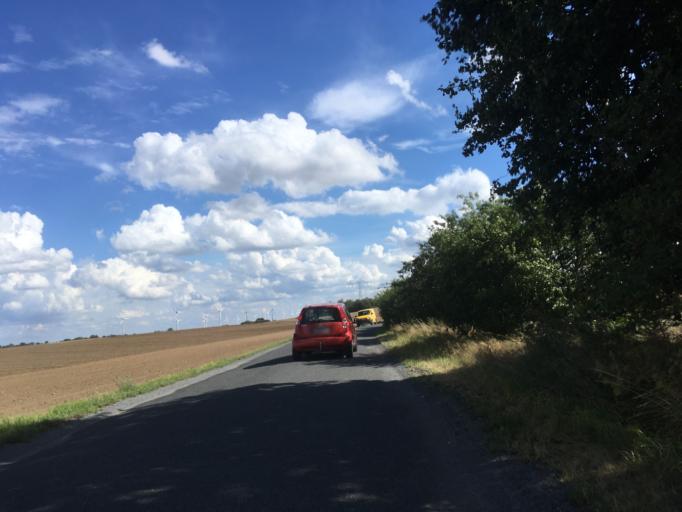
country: DE
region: Brandenburg
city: Angermunde
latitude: 52.9674
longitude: 13.9982
